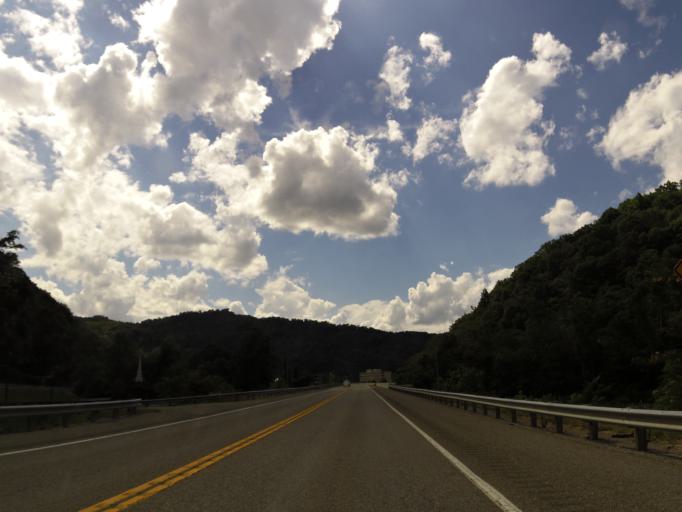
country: US
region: Kentucky
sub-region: Harlan County
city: Harlan
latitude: 36.8075
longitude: -83.3065
